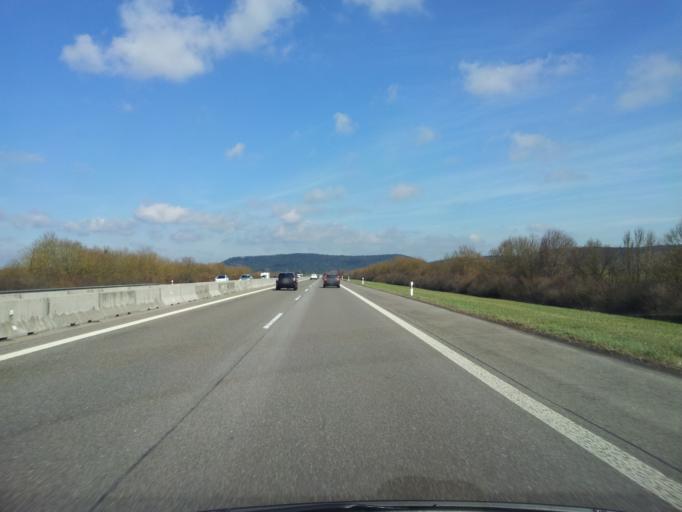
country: DE
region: Baden-Wuerttemberg
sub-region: Freiburg Region
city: Epfendorf
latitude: 48.2537
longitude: 8.6435
